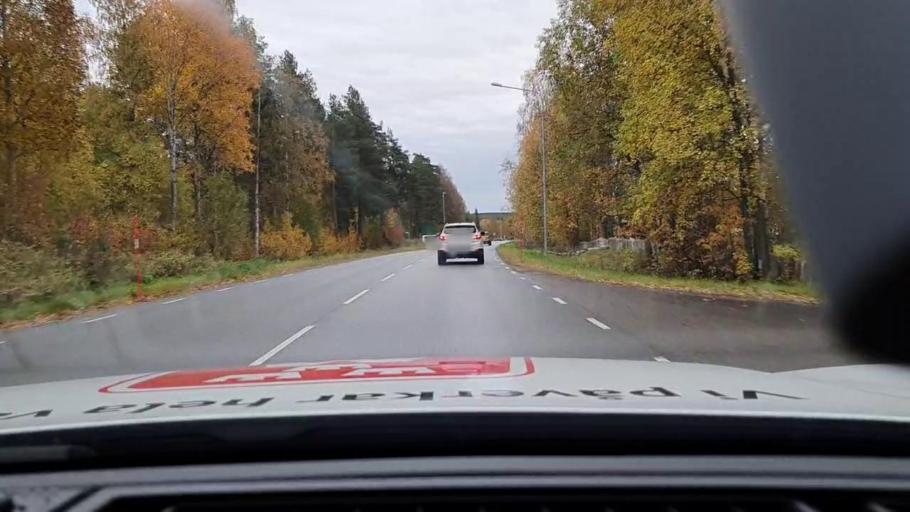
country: SE
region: Norrbotten
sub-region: Bodens Kommun
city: Saevast
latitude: 65.7696
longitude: 21.7341
